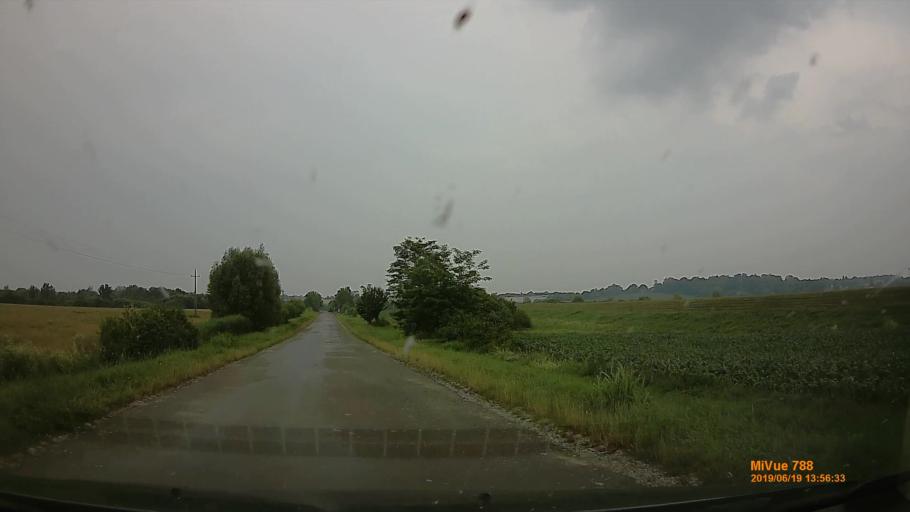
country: HU
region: Baranya
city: Szigetvar
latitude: 46.0822
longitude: 17.8116
